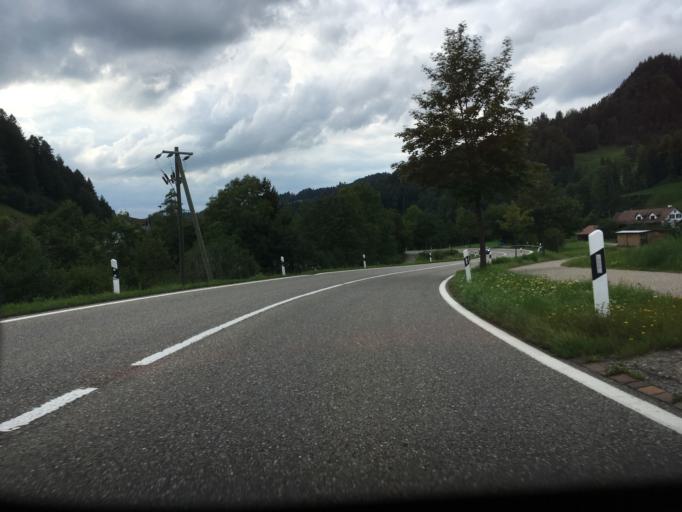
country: CH
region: Zurich
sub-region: Bezirk Pfaeffikon
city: Bauma
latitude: 47.3603
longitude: 8.9159
